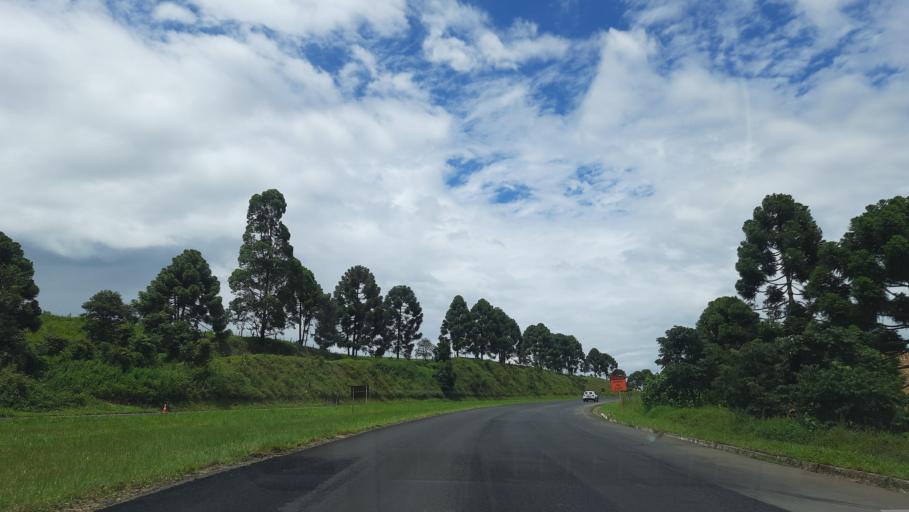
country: BR
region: Minas Gerais
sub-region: Pocos De Caldas
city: Pocos de Caldas
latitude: -21.8252
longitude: -46.6714
